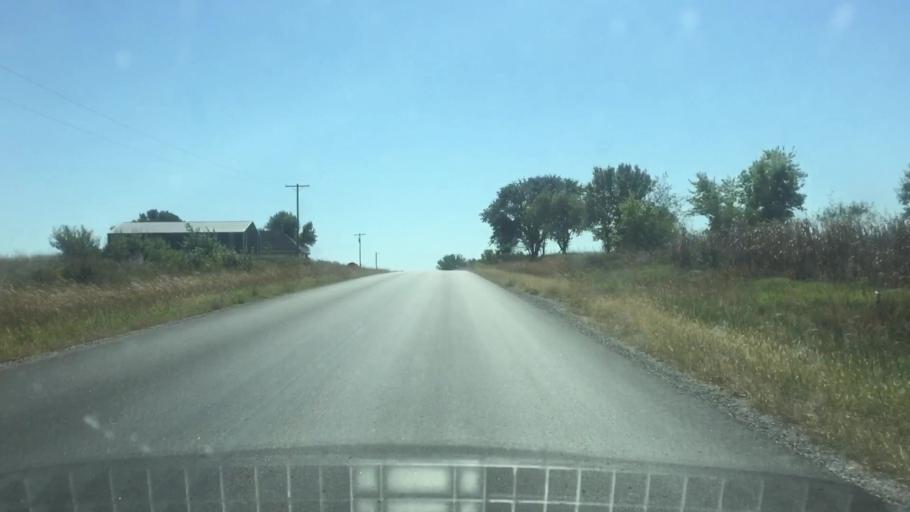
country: US
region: Kansas
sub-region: Marshall County
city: Marysville
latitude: 39.9547
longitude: -96.6008
